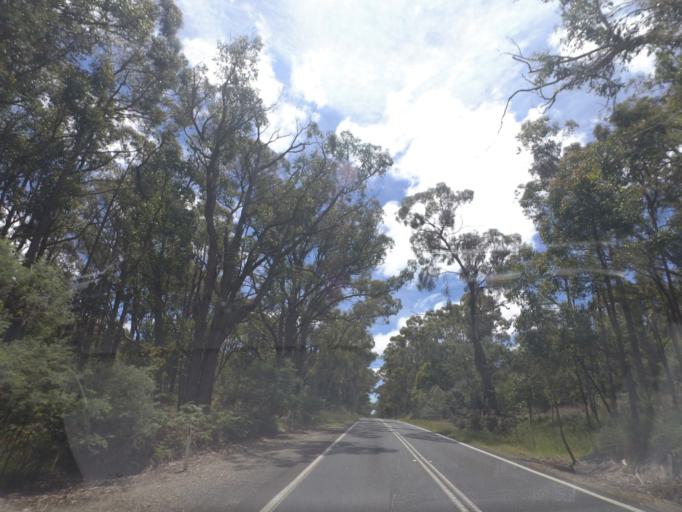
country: AU
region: Victoria
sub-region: Mount Alexander
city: Castlemaine
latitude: -37.3105
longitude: 144.1656
